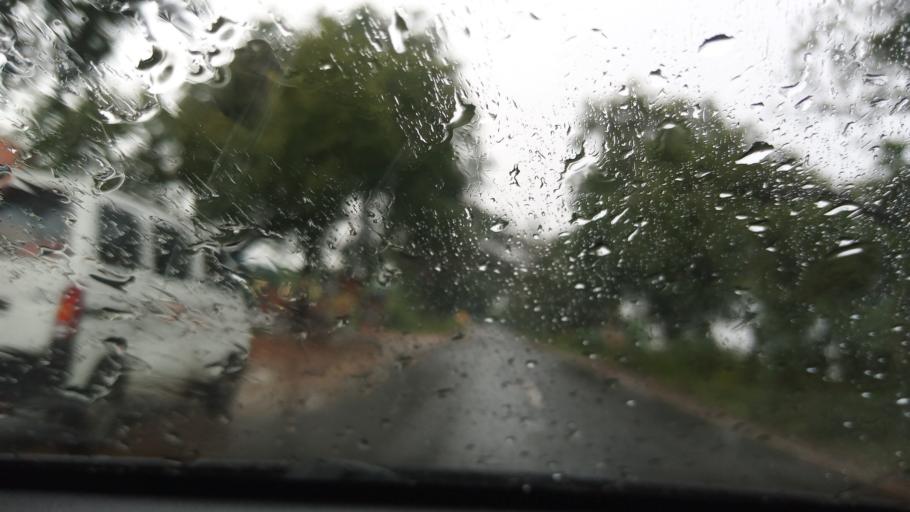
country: IN
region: Tamil Nadu
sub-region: Vellore
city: Kalavai
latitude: 12.8008
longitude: 79.4364
